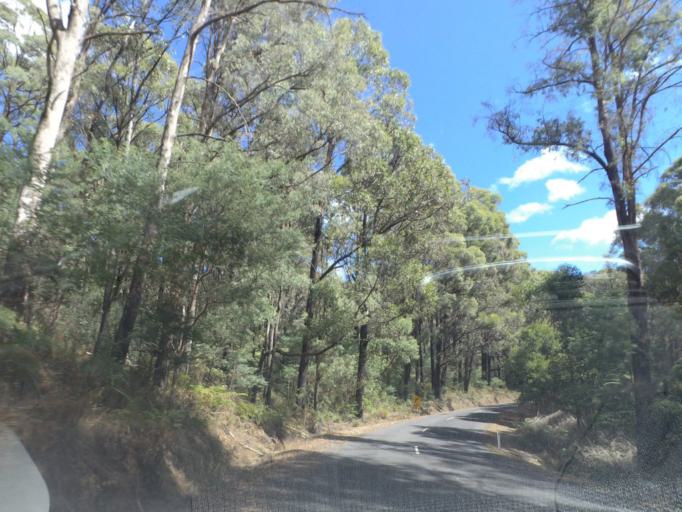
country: AU
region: Victoria
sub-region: Murrindindi
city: Alexandra
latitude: -37.3363
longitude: 145.9520
